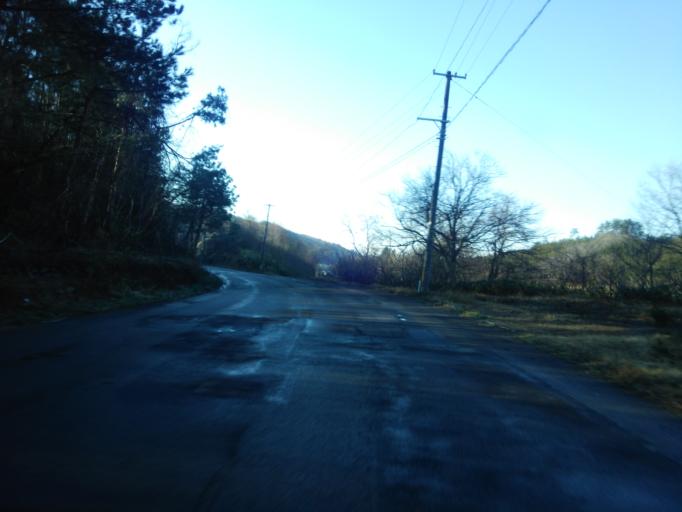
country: JP
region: Fukushima
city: Kitakata
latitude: 37.7006
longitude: 139.7871
